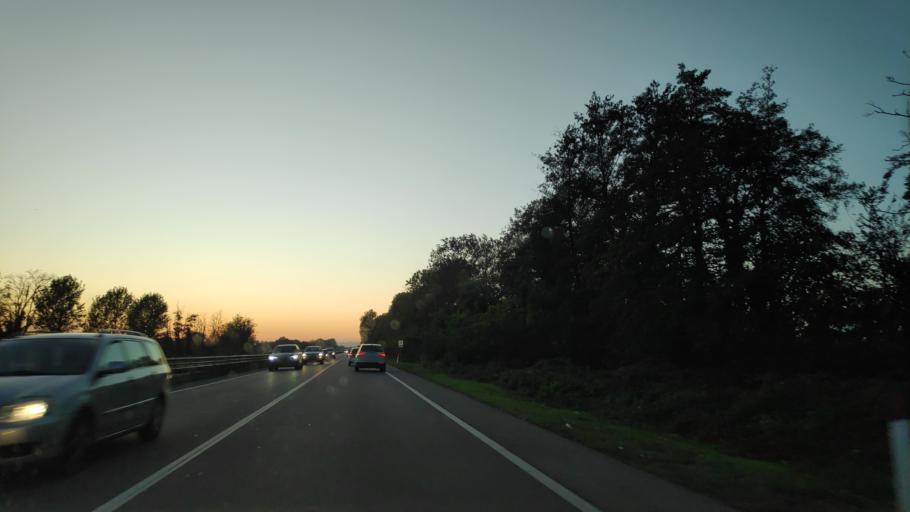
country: IT
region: Lombardy
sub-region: Citta metropolitana di Milano
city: Vermezzo
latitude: 45.4038
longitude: 8.9909
